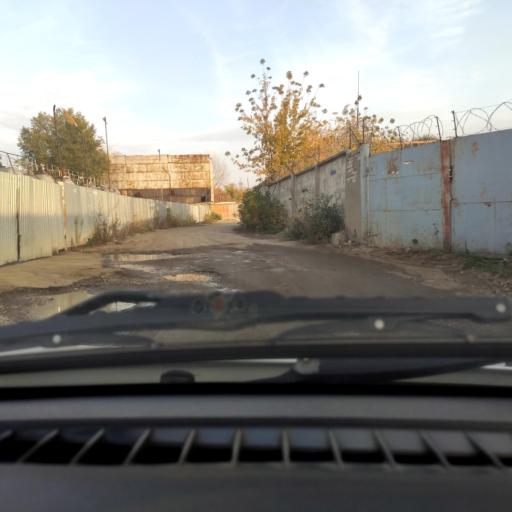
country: RU
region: Samara
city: Tol'yatti
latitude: 53.5284
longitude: 49.4645
